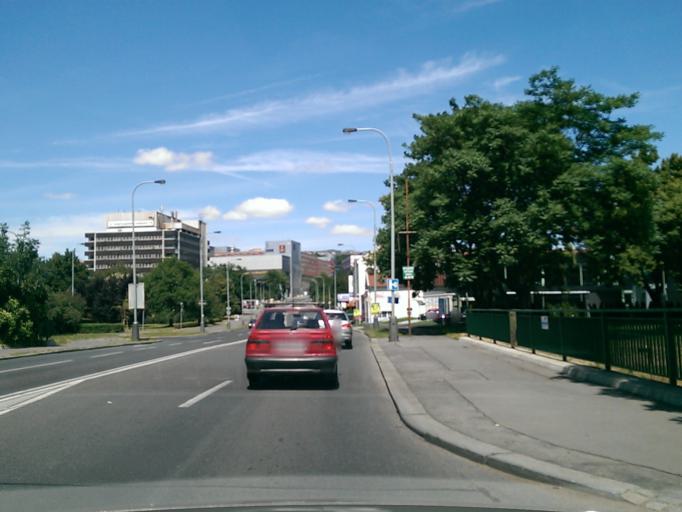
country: CZ
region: Praha
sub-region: Praha 9
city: Prosek
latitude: 50.1060
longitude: 14.5027
